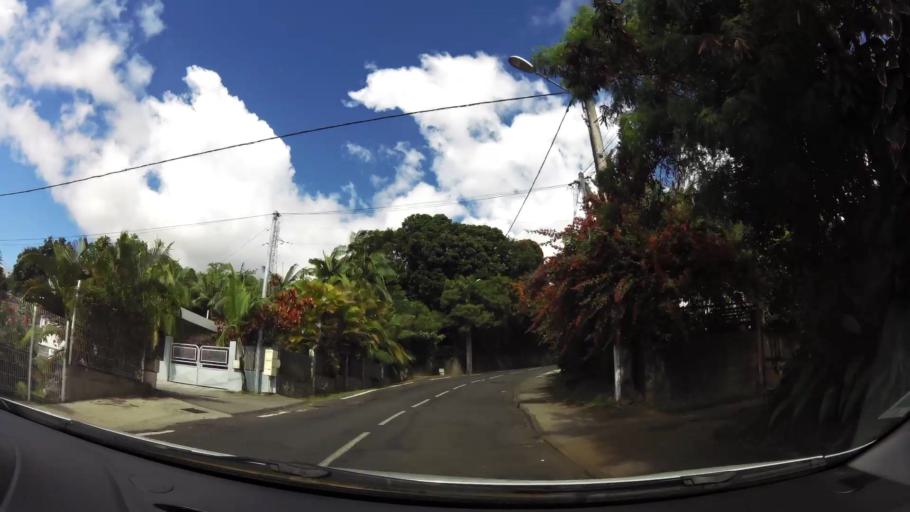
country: RE
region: Reunion
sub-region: Reunion
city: Saint-Denis
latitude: -20.9286
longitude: 55.4931
